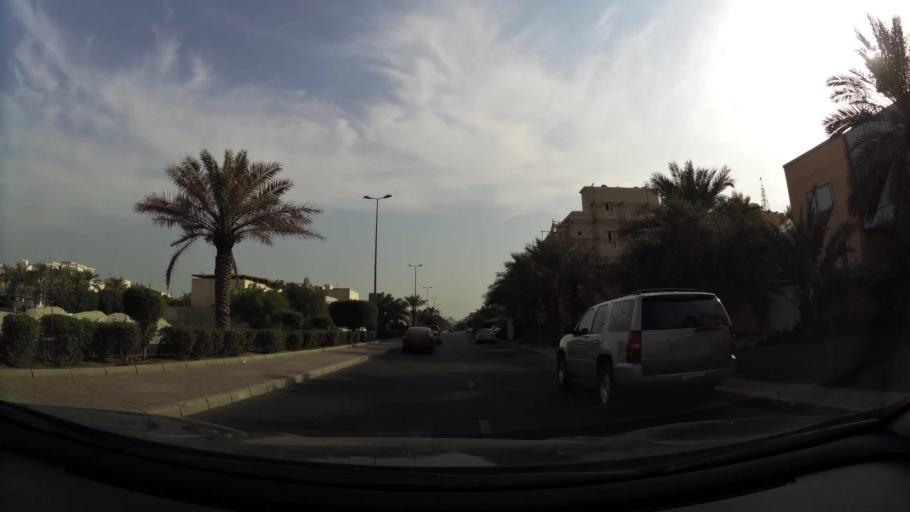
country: KW
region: Muhafazat Hawalli
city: Hawalli
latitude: 29.3277
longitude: 48.0020
